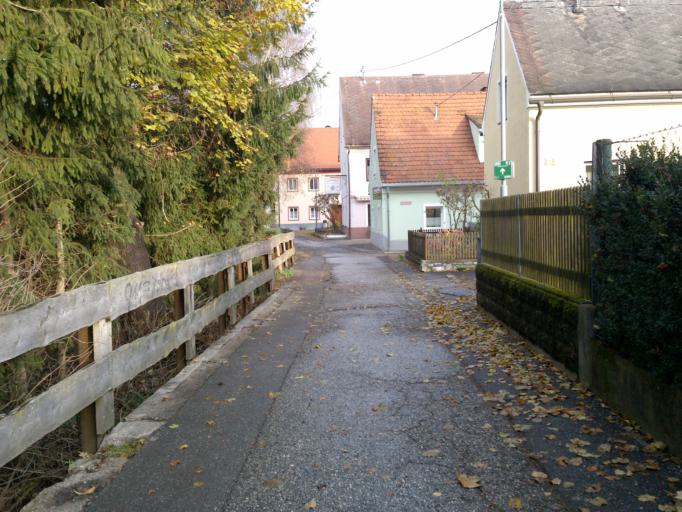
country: AT
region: Styria
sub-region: Politischer Bezirk Murtal
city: Judenburg
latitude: 47.1722
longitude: 14.6775
